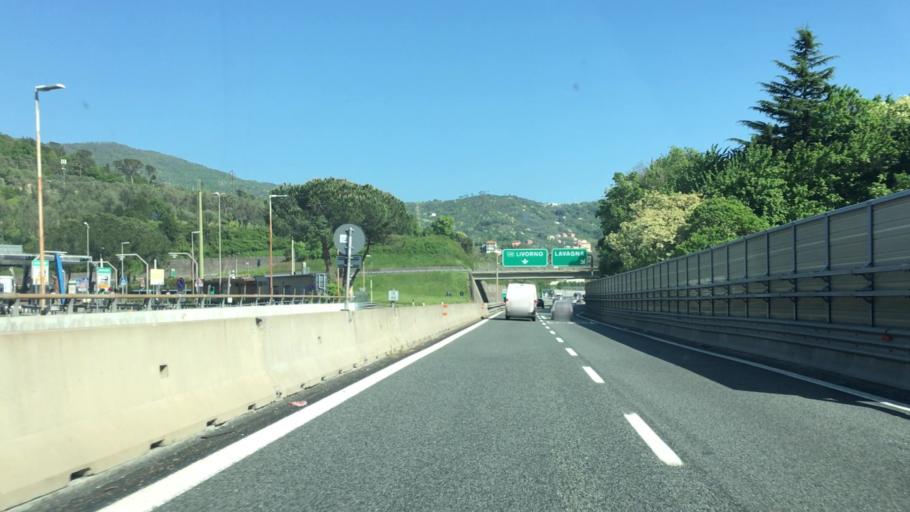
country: IT
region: Liguria
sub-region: Provincia di Genova
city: Lavagna
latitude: 44.3185
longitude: 9.3476
